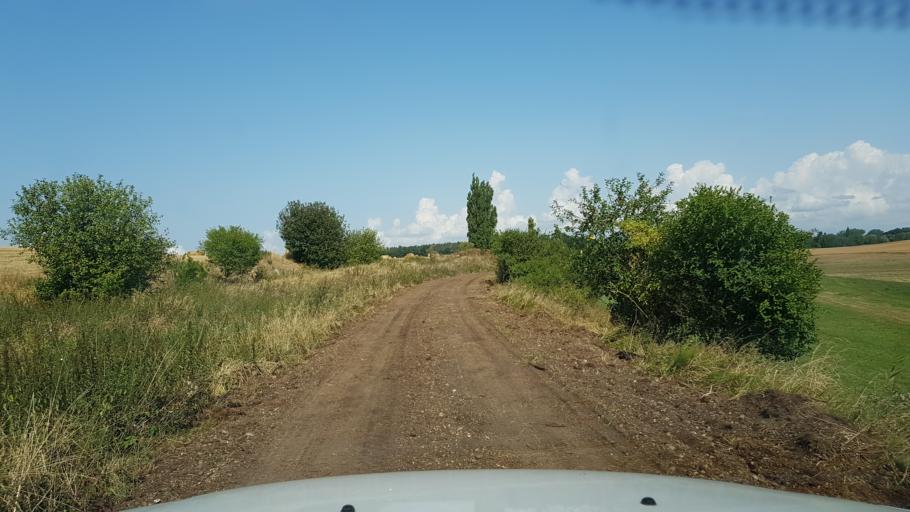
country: PL
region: West Pomeranian Voivodeship
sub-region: Powiat choszczenski
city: Pelczyce
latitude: 53.0784
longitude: 15.3048
